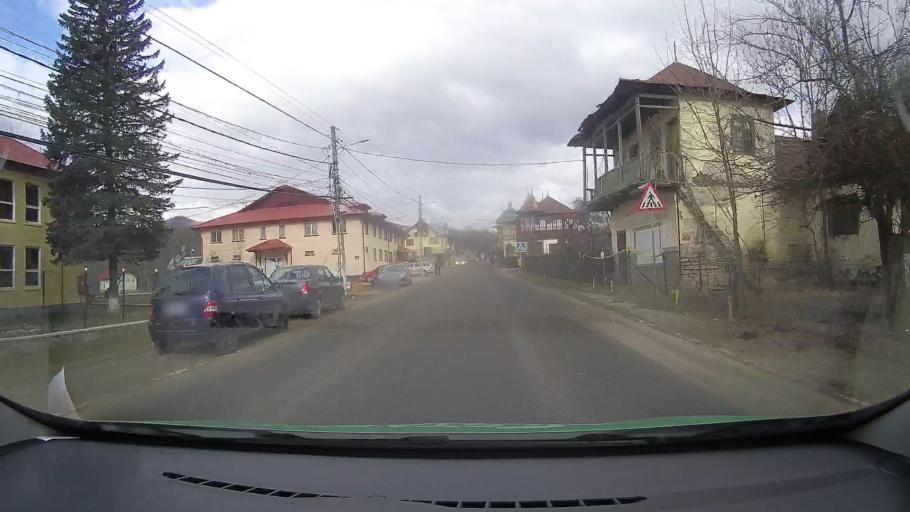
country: RO
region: Prahova
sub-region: Comuna Provita de Sus
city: Provita de Sus
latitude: 45.1360
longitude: 25.6360
